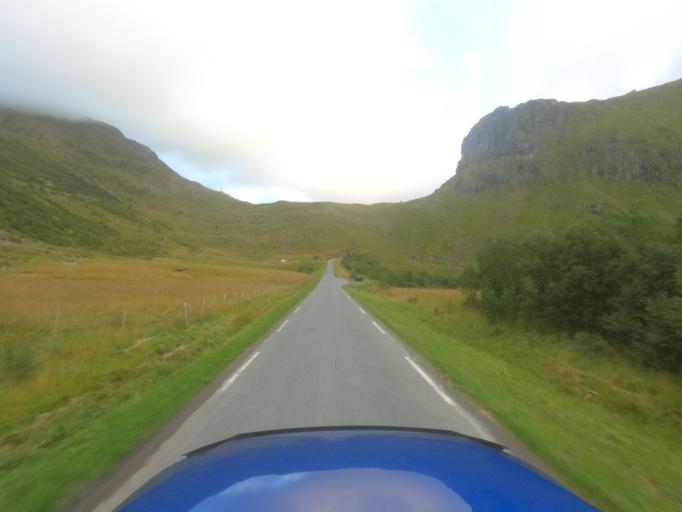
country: NO
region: Nordland
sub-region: Vestvagoy
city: Leknes
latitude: 68.2605
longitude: 13.6019
